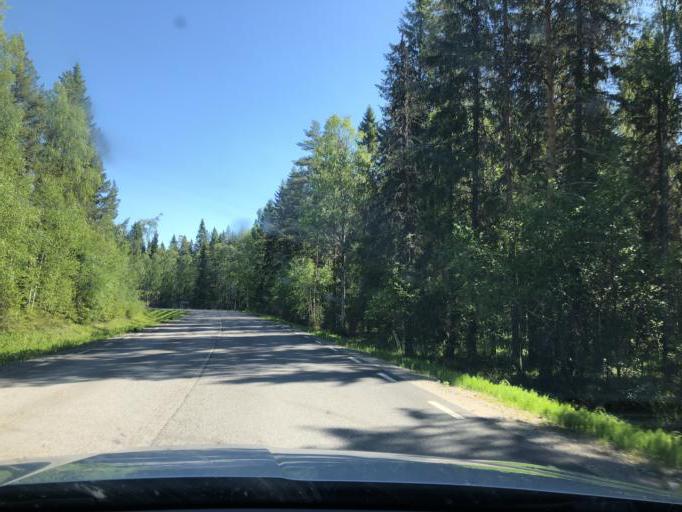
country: SE
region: Norrbotten
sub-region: Lulea Kommun
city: Gammelstad
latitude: 65.6566
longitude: 22.0486
